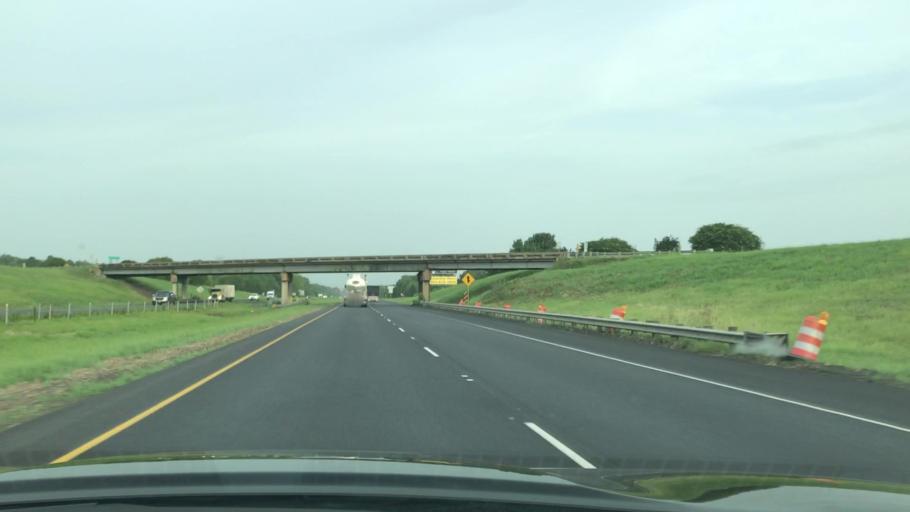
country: US
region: Louisiana
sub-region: Caddo Parish
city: Greenwood
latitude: 32.4441
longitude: -93.9482
